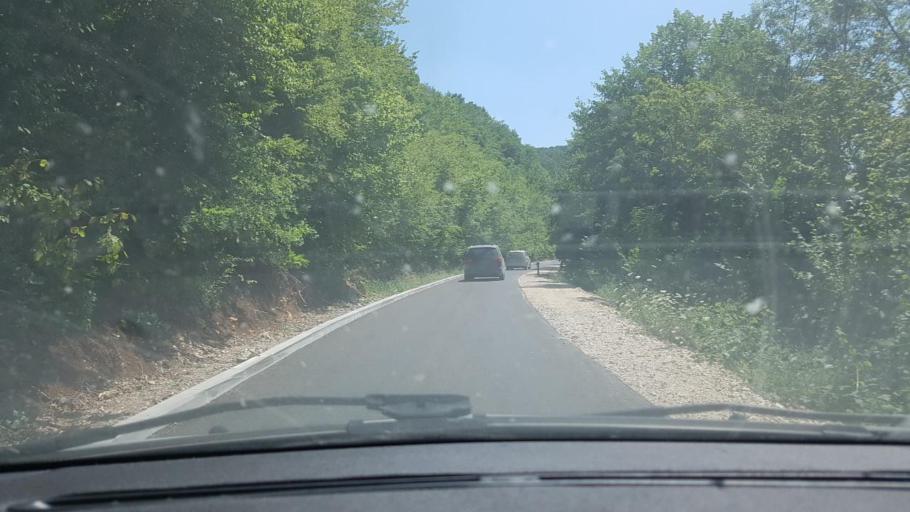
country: BA
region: Federation of Bosnia and Herzegovina
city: Orasac
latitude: 44.6253
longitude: 16.0554
